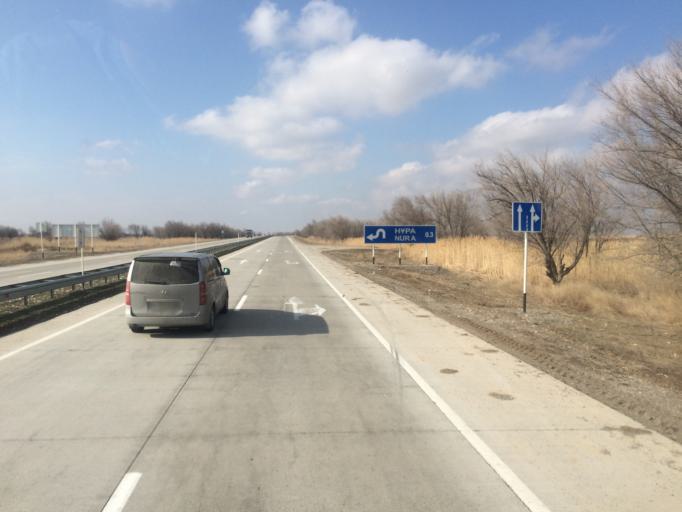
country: KZ
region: Ongtustik Qazaqstan
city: Bayaldyr
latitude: 43.0082
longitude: 68.7751
